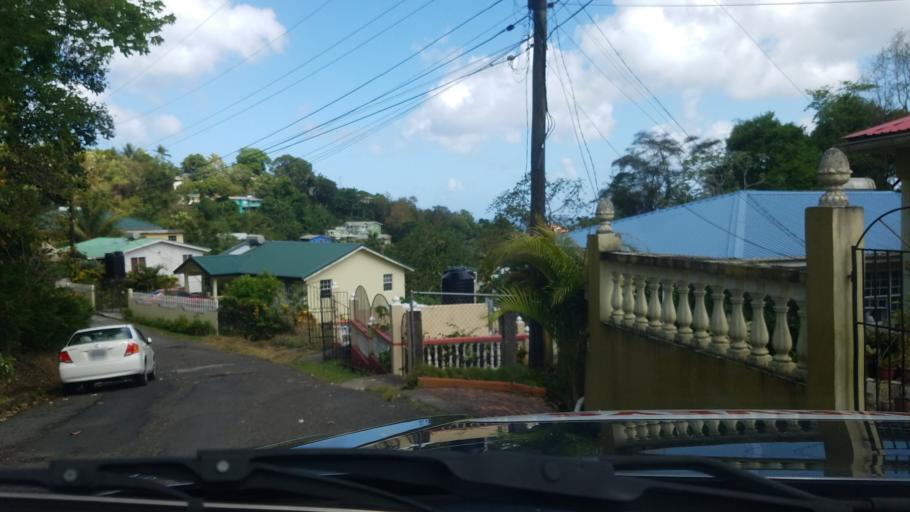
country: LC
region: Castries Quarter
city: Bisee
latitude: 14.0160
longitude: -60.9812
